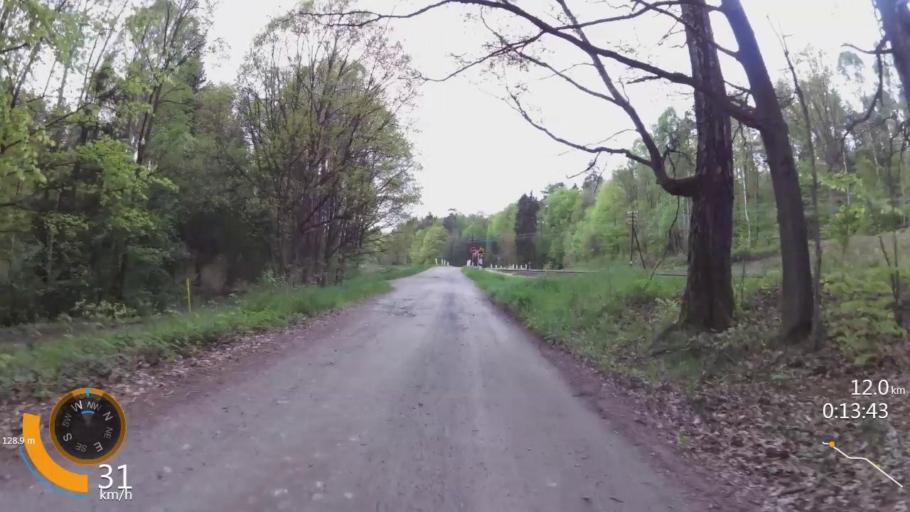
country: PL
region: West Pomeranian Voivodeship
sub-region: Powiat drawski
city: Wierzchowo
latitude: 53.5272
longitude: 16.0968
